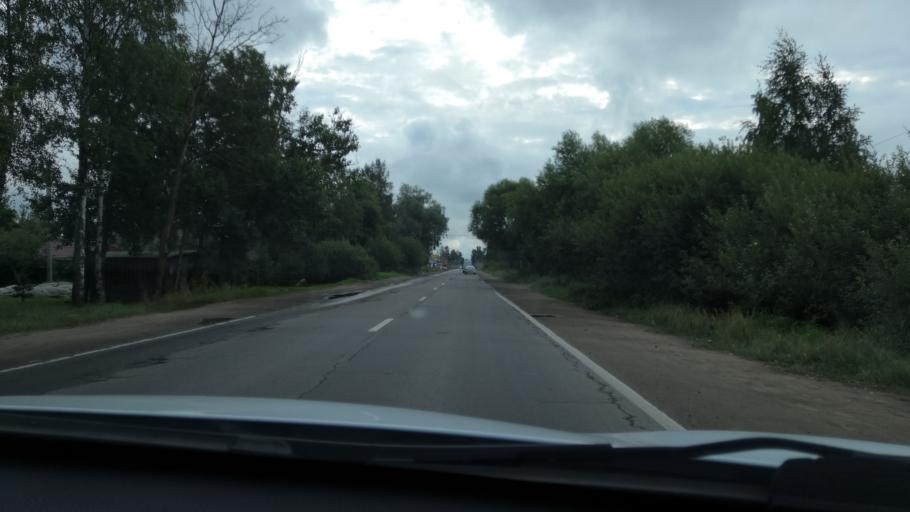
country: RU
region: St.-Petersburg
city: Kolpino
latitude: 59.7046
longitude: 30.5703
